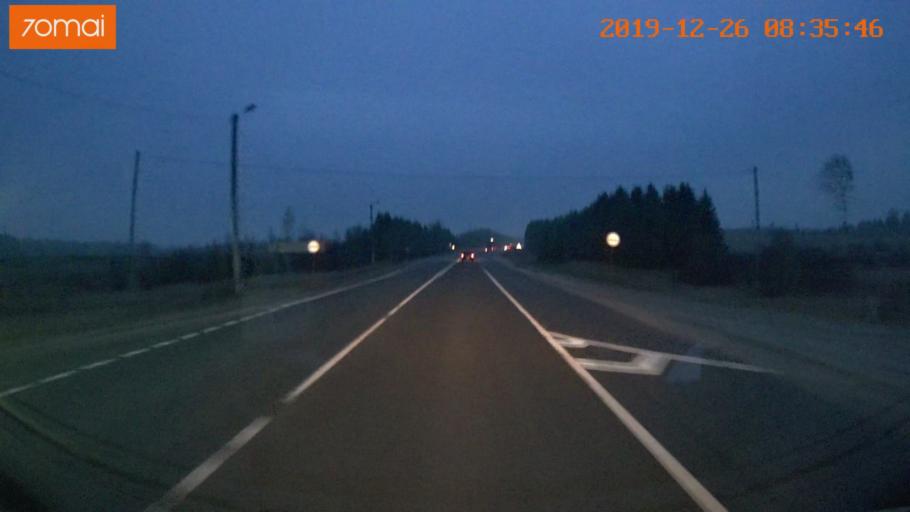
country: RU
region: Jaroslavl
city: Prechistoye
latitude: 58.4838
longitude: 40.3246
